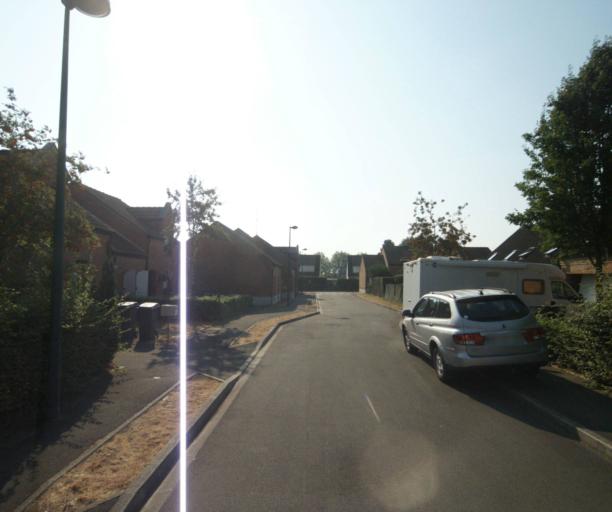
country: FR
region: Nord-Pas-de-Calais
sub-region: Departement du Nord
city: Quesnoy-sur-Deule
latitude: 50.7160
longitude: 3.0066
